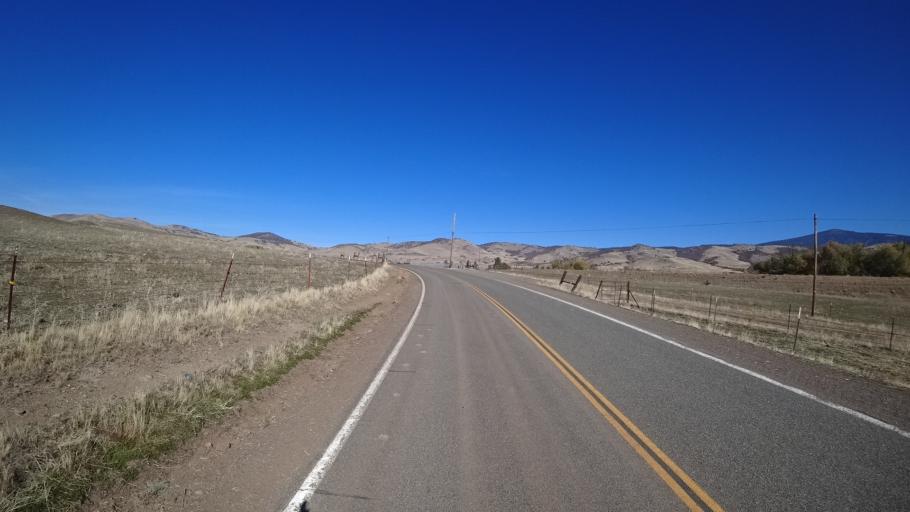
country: US
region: California
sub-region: Siskiyou County
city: Montague
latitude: 41.8098
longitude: -122.3768
